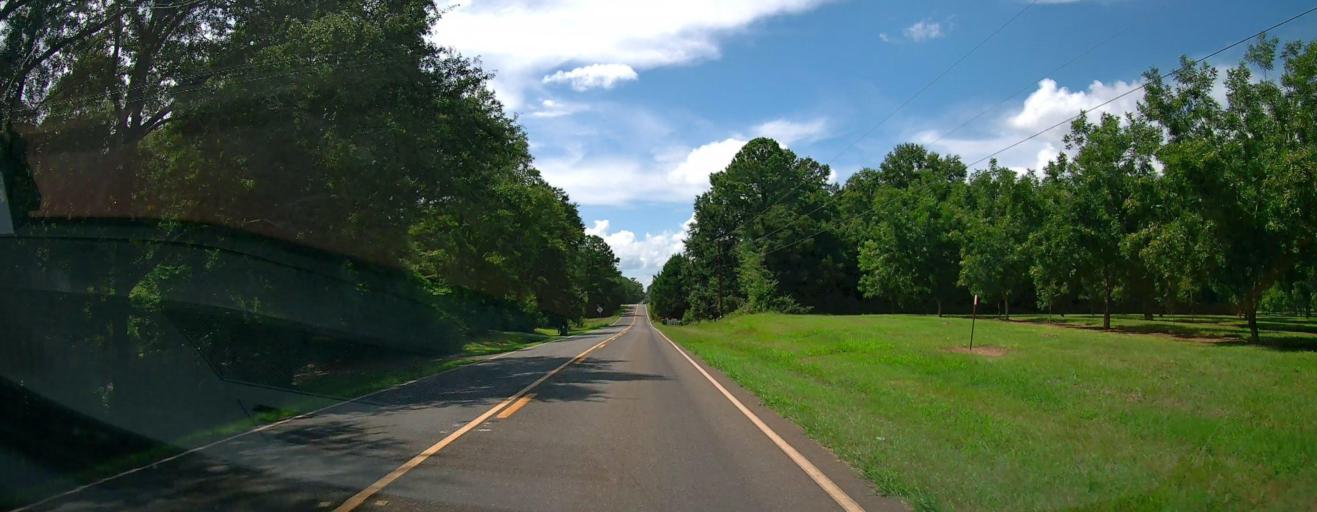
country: US
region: Georgia
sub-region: Macon County
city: Marshallville
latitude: 32.4562
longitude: -83.9254
